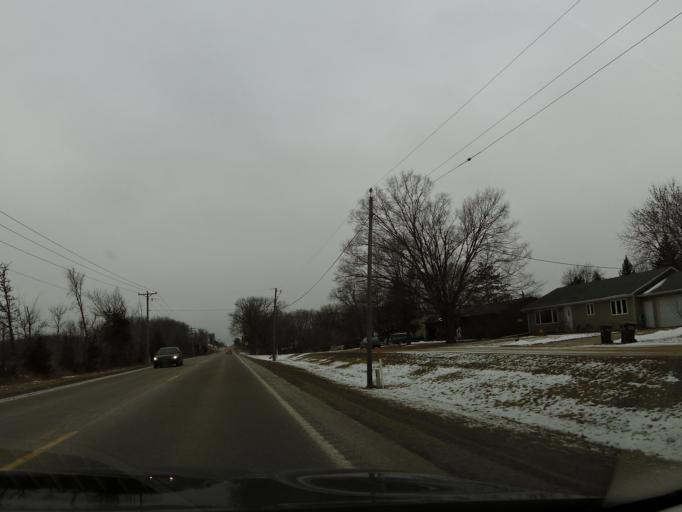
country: US
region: Minnesota
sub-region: Carver County
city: Waconia
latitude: 44.8221
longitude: -93.7884
